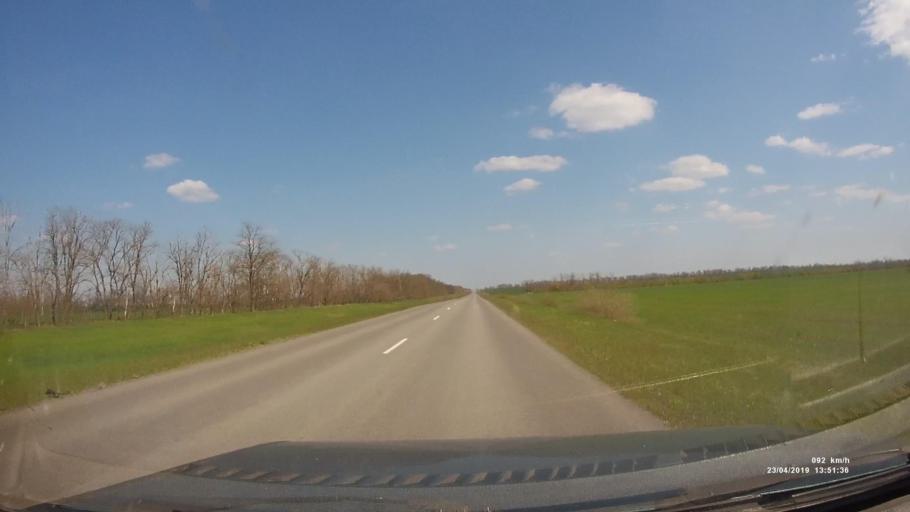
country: RU
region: Kalmykiya
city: Yashalta
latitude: 46.5995
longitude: 42.9374
